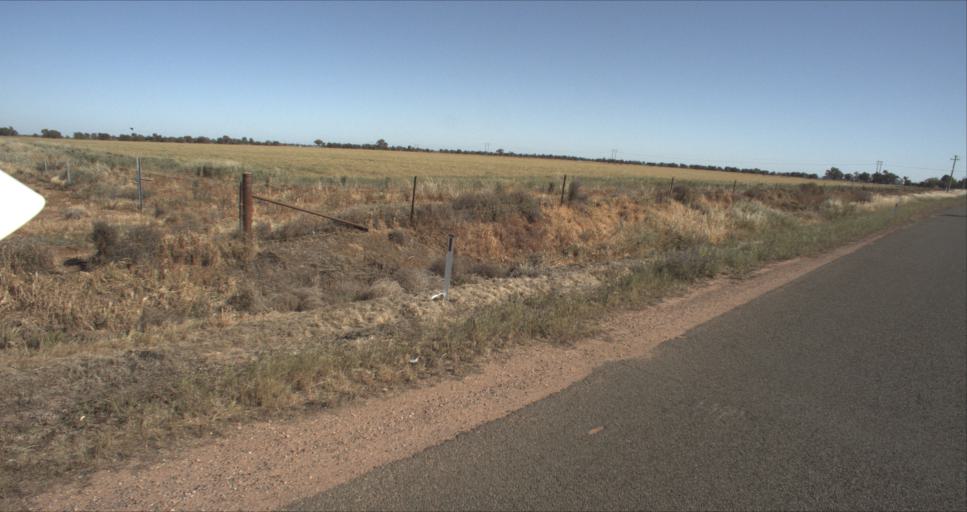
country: AU
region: New South Wales
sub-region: Leeton
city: Leeton
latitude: -34.5635
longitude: 146.2649
